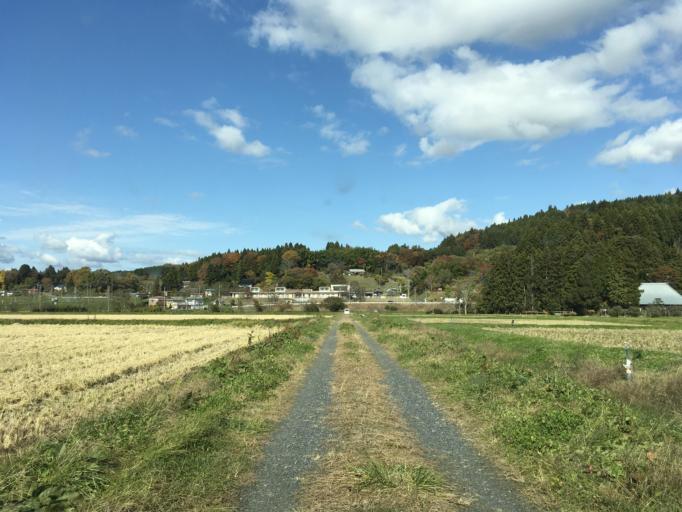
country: JP
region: Iwate
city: Ichinoseki
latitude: 38.9559
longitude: 141.3707
